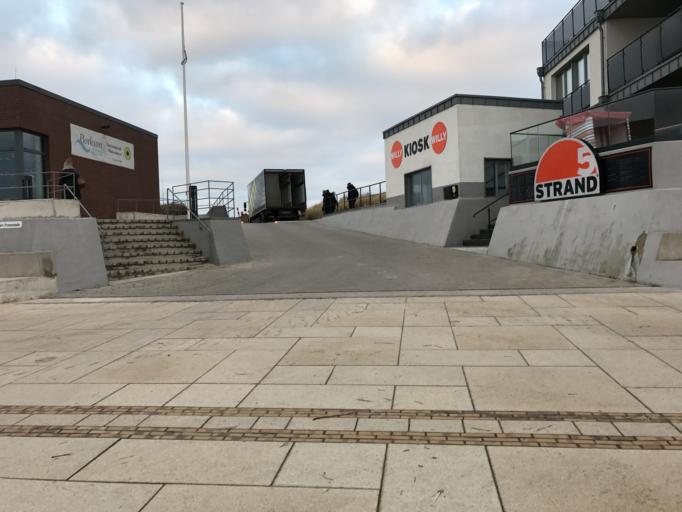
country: DE
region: Lower Saxony
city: Borkum
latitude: 53.5804
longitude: 6.6621
